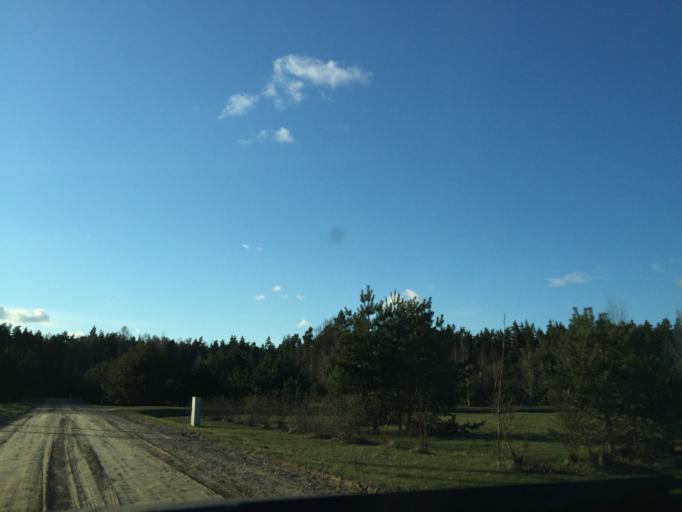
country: LV
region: Kekava
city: Kekava
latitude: 56.8528
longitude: 24.2354
